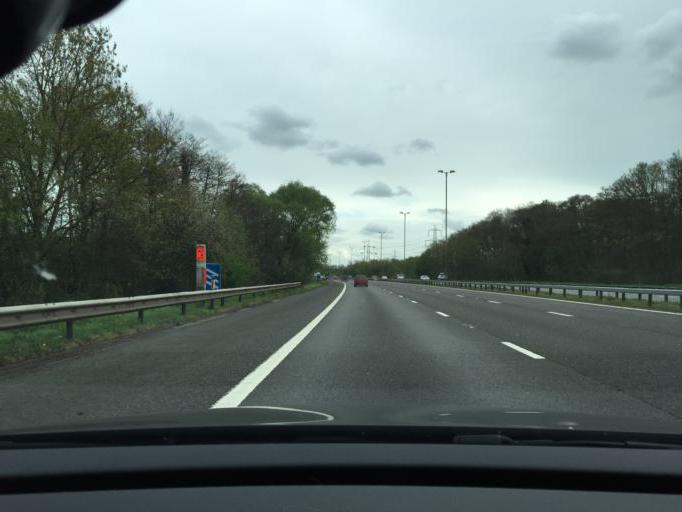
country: GB
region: England
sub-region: West Berkshire
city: Theale
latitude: 51.4457
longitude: -1.0731
